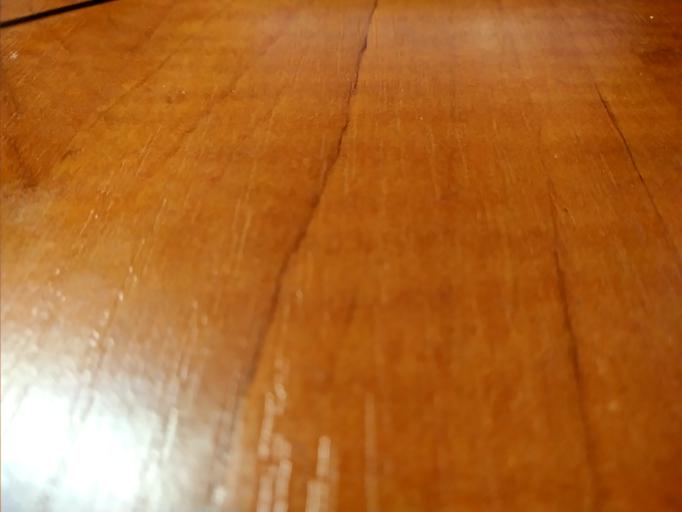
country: RU
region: Tverskaya
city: Spirovo
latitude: 57.3750
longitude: 34.9786
